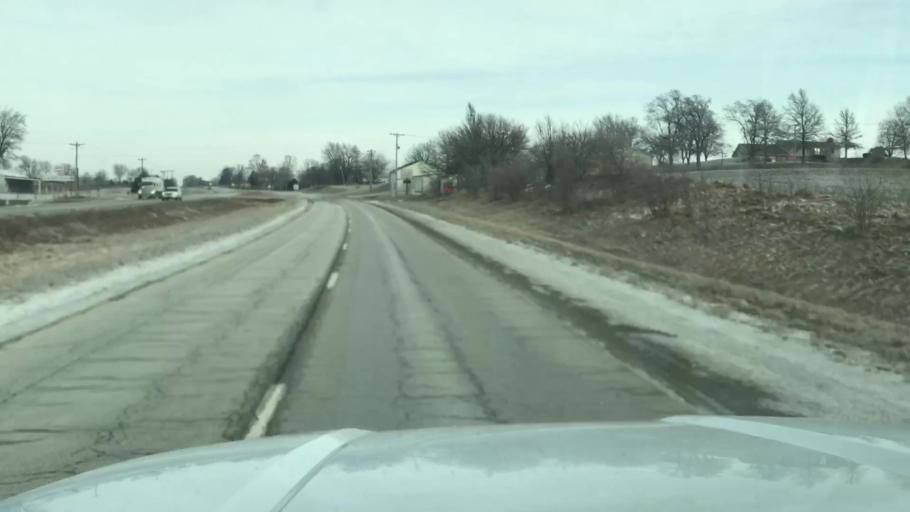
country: US
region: Missouri
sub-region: Andrew County
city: Country Club Village
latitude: 39.8637
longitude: -94.8086
